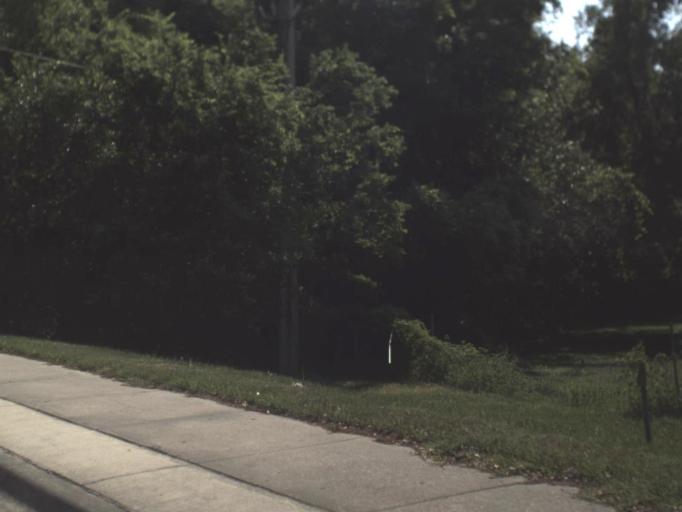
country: US
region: Florida
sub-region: Duval County
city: Jacksonville
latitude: 30.2948
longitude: -81.7530
